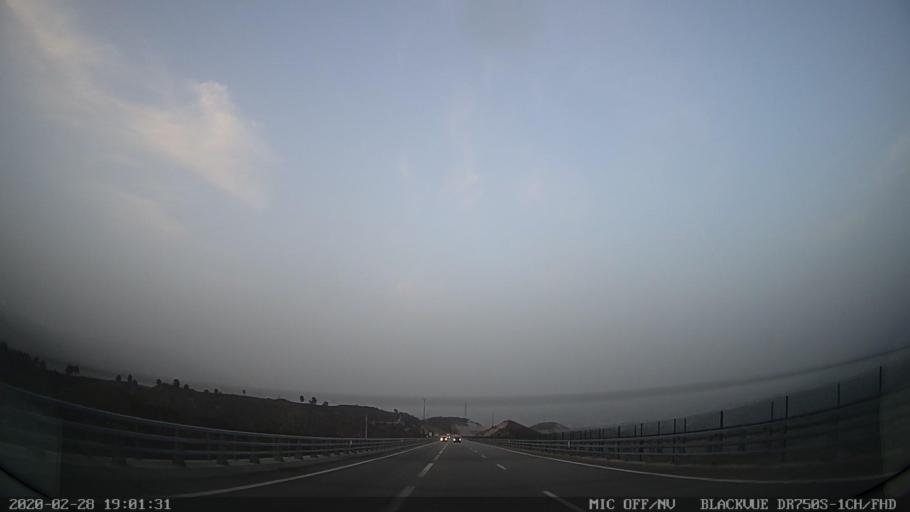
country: PT
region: Vila Real
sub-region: Vila Real
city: Vila Real
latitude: 41.2665
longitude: -7.7865
